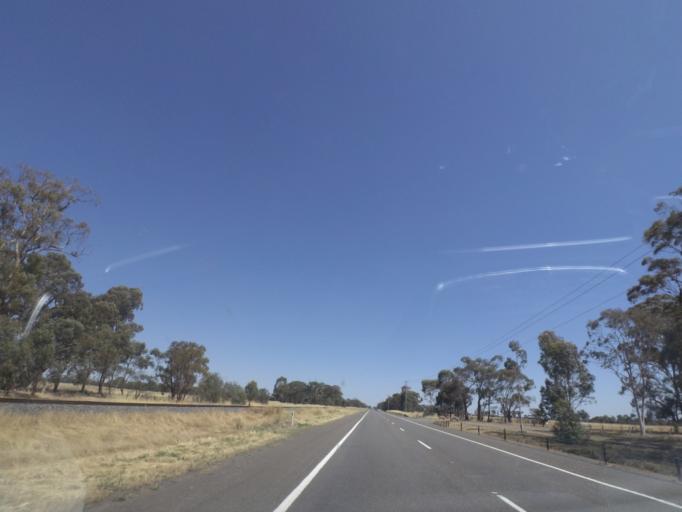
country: AU
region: Victoria
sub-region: Greater Shepparton
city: Shepparton
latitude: -36.2445
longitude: 145.4319
